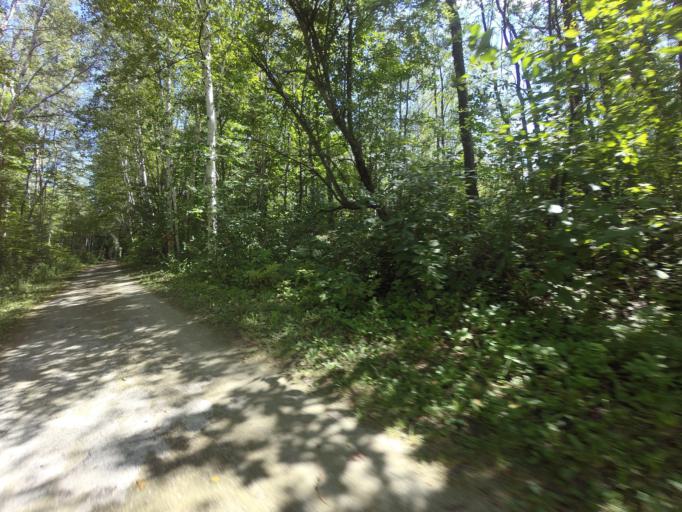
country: CA
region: Ontario
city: Orangeville
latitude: 43.7848
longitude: -80.1536
